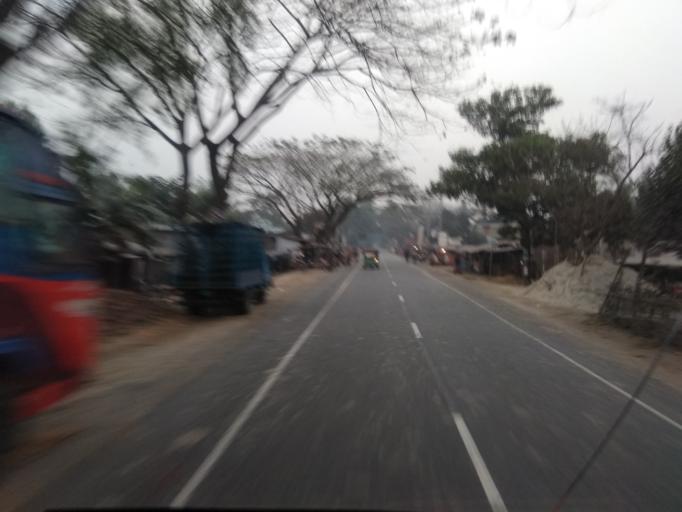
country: BD
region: Rajshahi
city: Bogra
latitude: 24.6779
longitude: 89.2847
